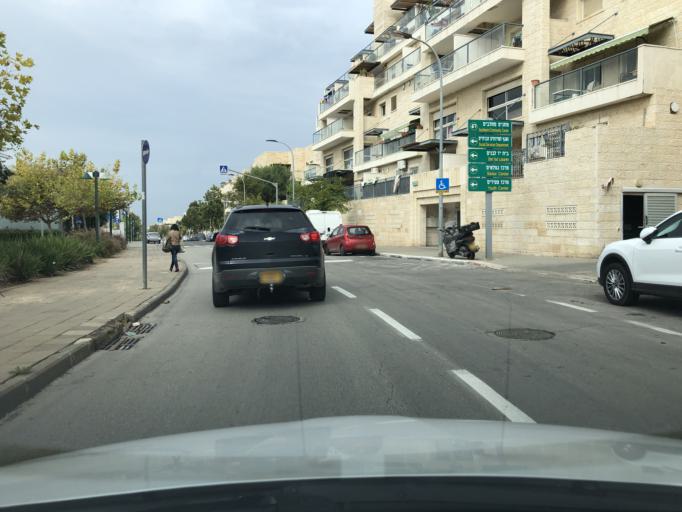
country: IL
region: Central District
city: Modiin
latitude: 31.9121
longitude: 35.0124
